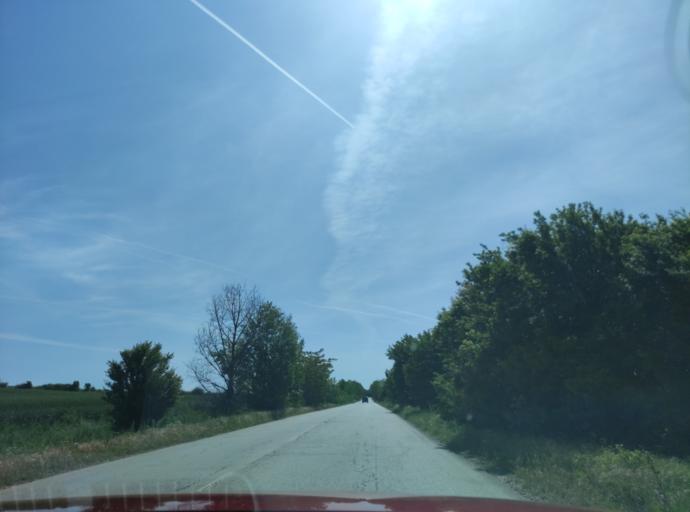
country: BG
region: Pleven
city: Iskur
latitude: 43.4494
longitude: 24.3191
